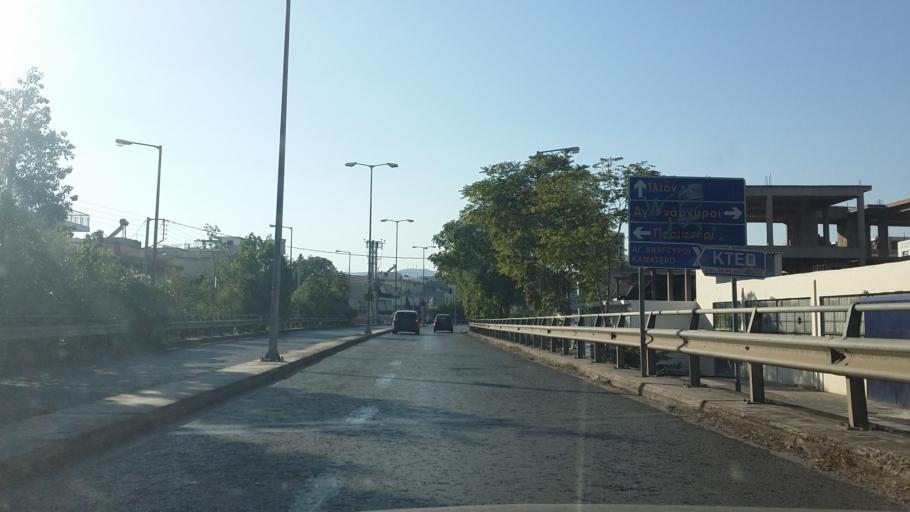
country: GR
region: Attica
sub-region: Nomarchia Athinas
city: Agioi Anargyroi
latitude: 38.0150
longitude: 23.7154
